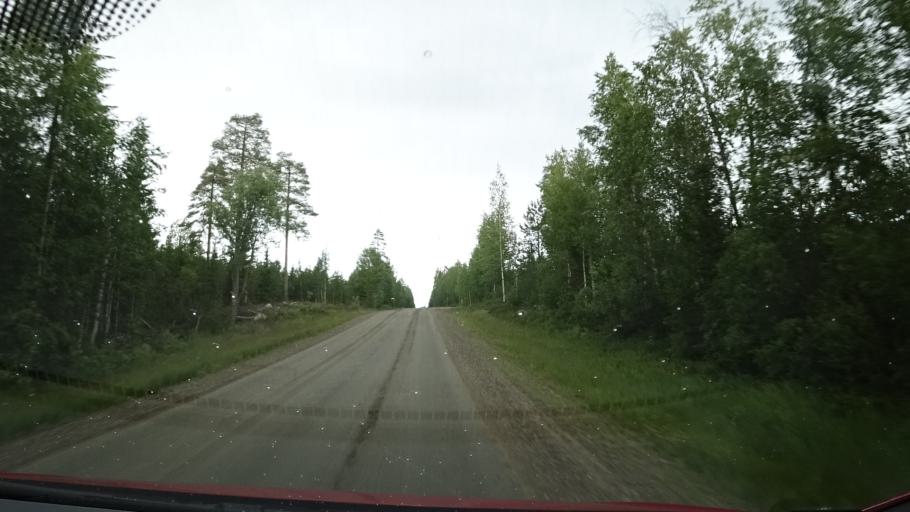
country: FI
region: Kainuu
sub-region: Kehys-Kainuu
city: Kuhmo
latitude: 63.9381
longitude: 29.2084
